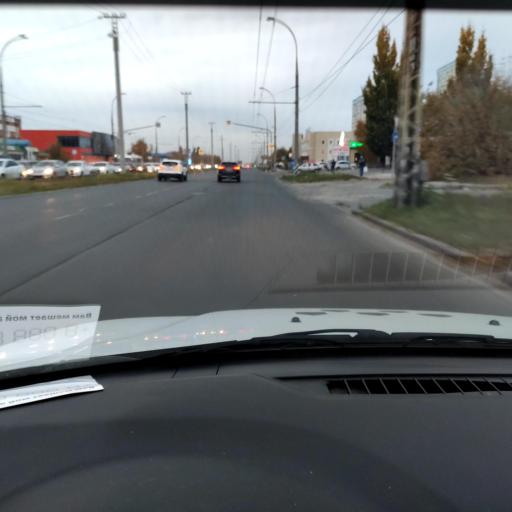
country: RU
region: Samara
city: Tol'yatti
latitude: 53.5380
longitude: 49.2997
